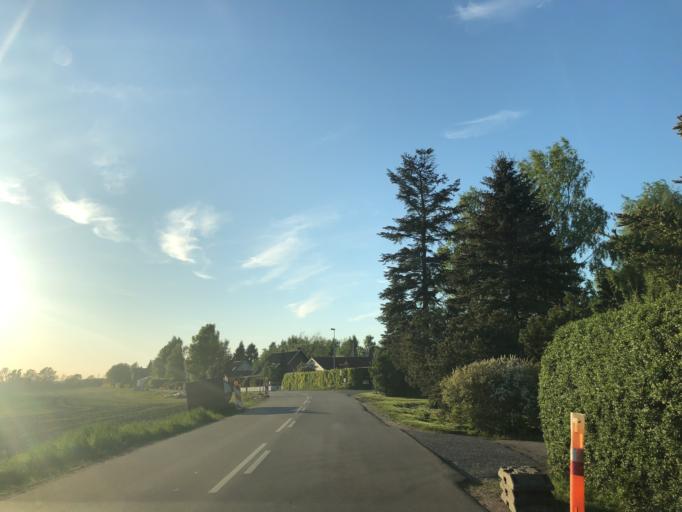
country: DK
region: Zealand
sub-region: Koge Kommune
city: Bjaeverskov
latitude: 55.4316
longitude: 12.0613
